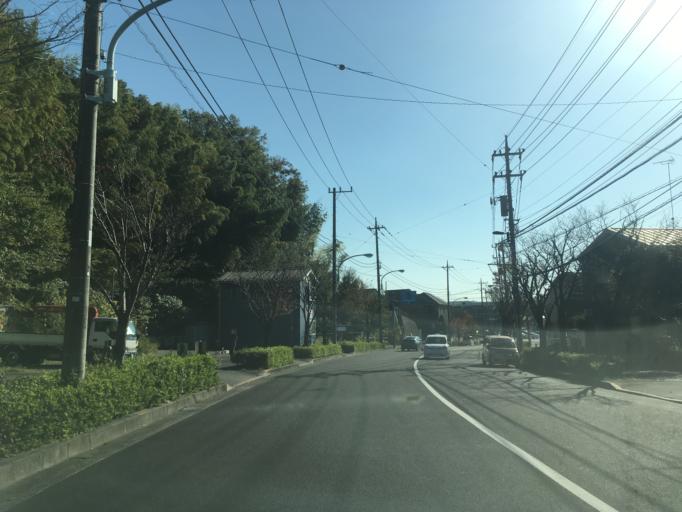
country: JP
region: Tokyo
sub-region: Machida-shi
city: Machida
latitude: 35.5839
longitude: 139.4226
